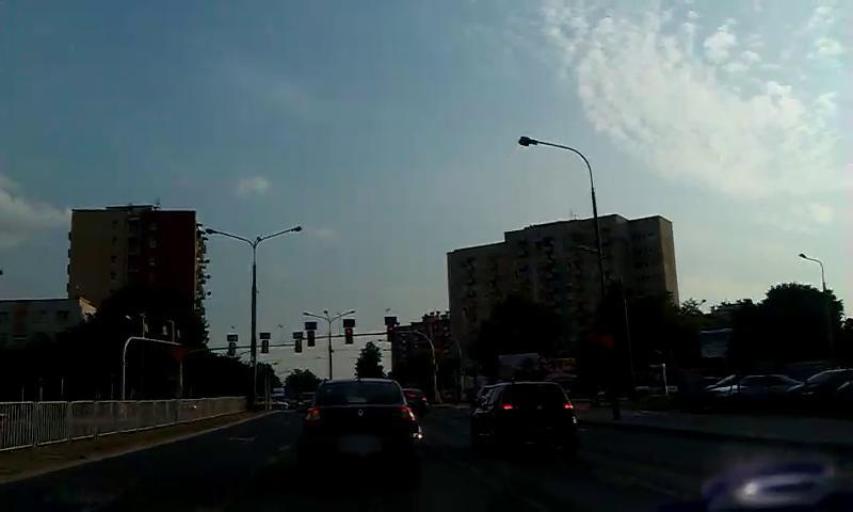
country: PL
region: Lublin Voivodeship
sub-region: Powiat lubelski
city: Lublin
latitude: 51.2320
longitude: 22.5915
